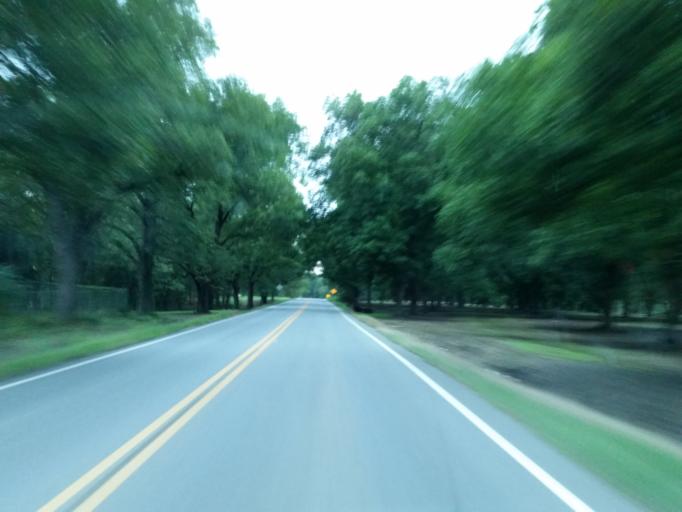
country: US
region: Georgia
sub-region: Crisp County
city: Cordele
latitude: 31.8637
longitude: -83.7467
